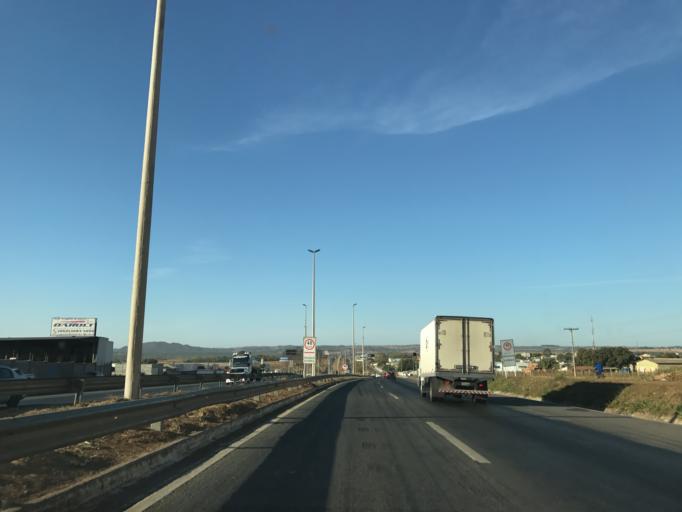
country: BR
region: Goias
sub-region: Aparecida De Goiania
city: Aparecida de Goiania
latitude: -16.8246
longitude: -49.2420
